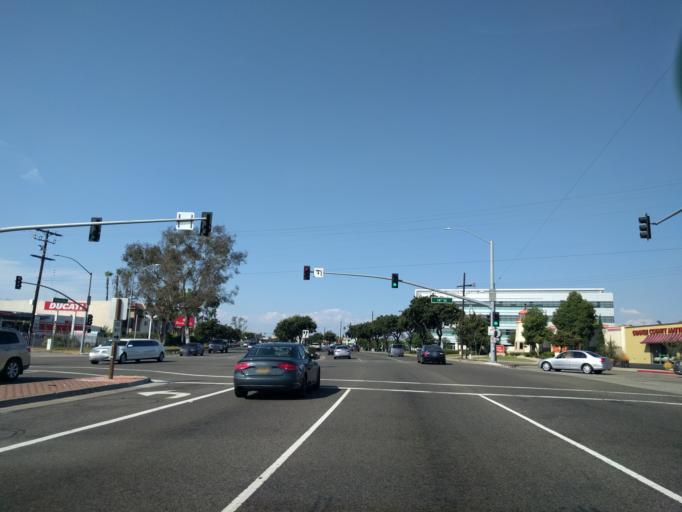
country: US
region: California
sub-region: Orange County
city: Costa Mesa
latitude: 33.6331
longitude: -117.9227
